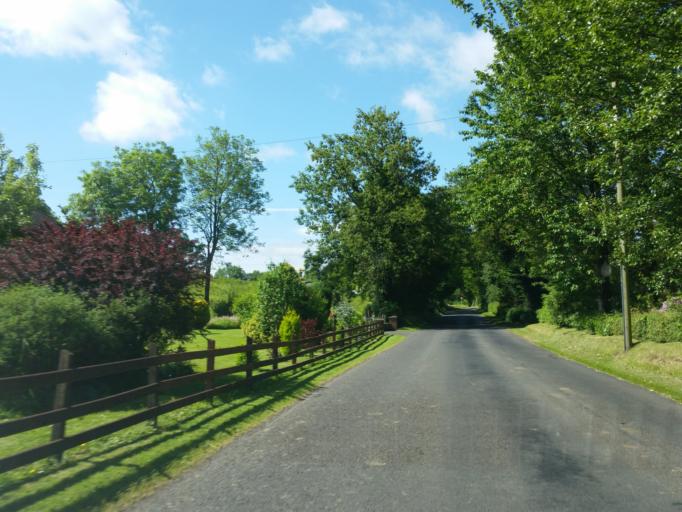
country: GB
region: Northern Ireland
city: Lisnaskea
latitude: 54.2945
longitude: -7.5381
